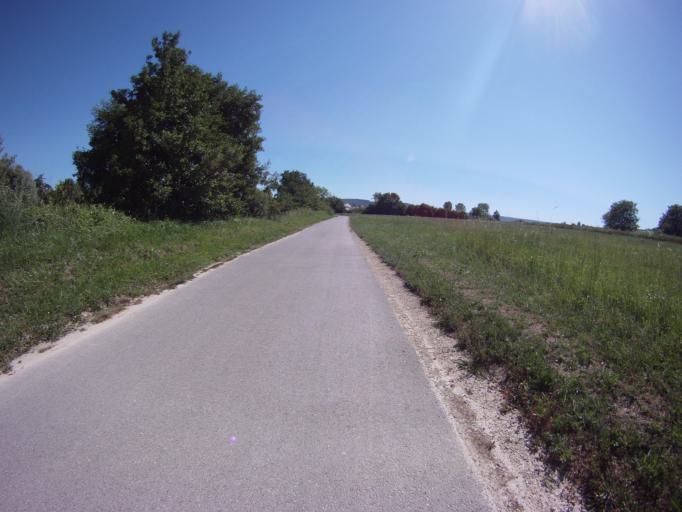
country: FR
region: Champagne-Ardenne
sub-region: Departement de la Marne
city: Dormans
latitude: 49.0848
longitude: 3.6395
